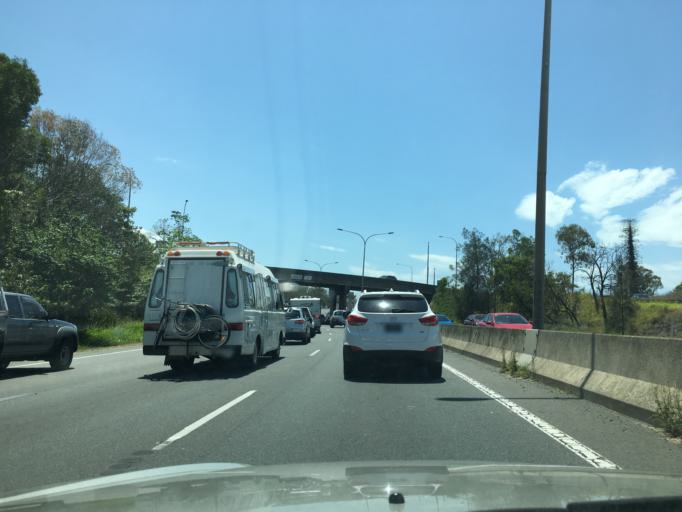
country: AU
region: Queensland
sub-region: Brisbane
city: Shorncliffe
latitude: -27.3749
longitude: 153.0966
